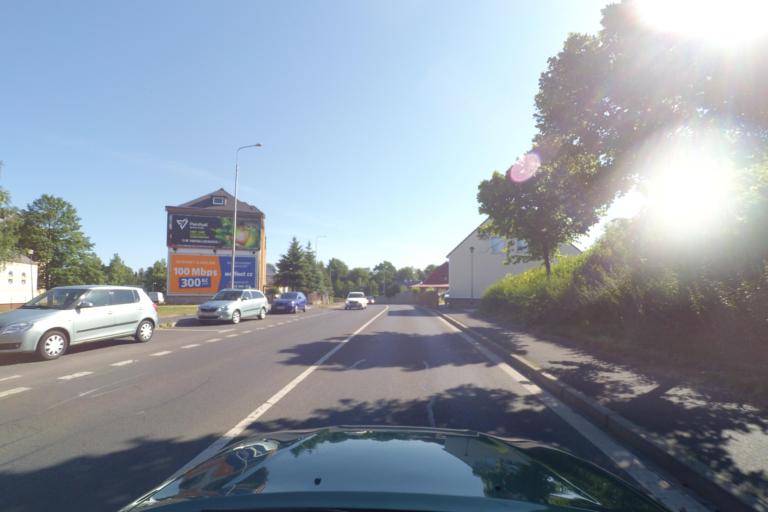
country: CZ
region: Karlovarsky
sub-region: Okres Sokolov
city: Sokolov
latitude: 50.1756
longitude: 12.6409
